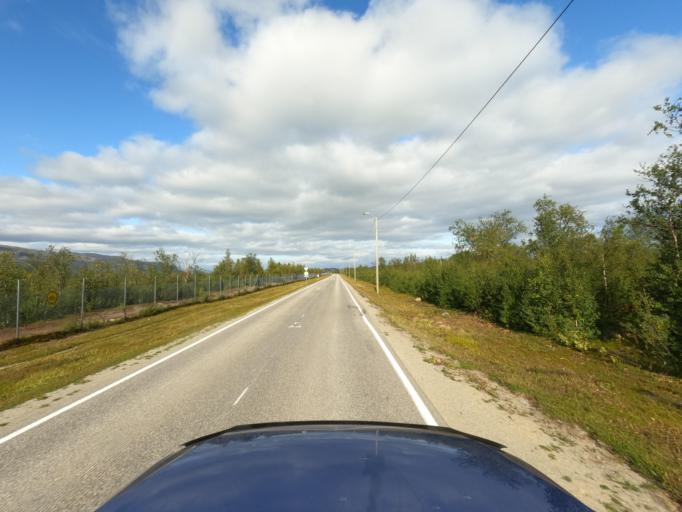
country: NO
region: Finnmark Fylke
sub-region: Porsanger
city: Lakselv
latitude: 70.0543
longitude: 24.9811
